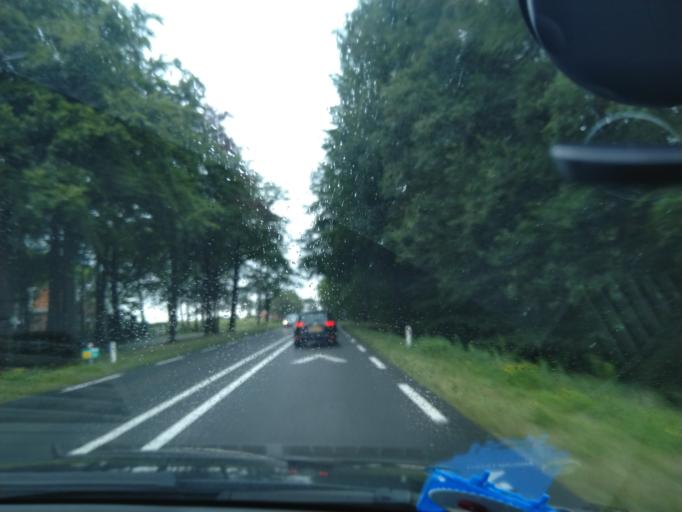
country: NL
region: Overijssel
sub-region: Gemeente Oldenzaal
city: Oldenzaal
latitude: 52.3455
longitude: 6.9693
